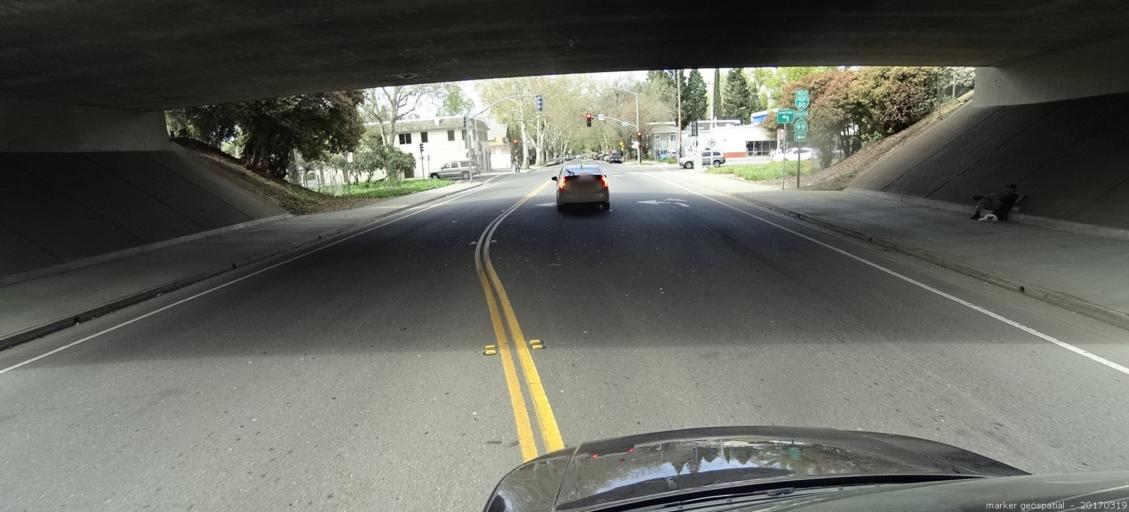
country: US
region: California
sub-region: Sacramento County
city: Sacramento
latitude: 38.5788
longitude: -121.4648
